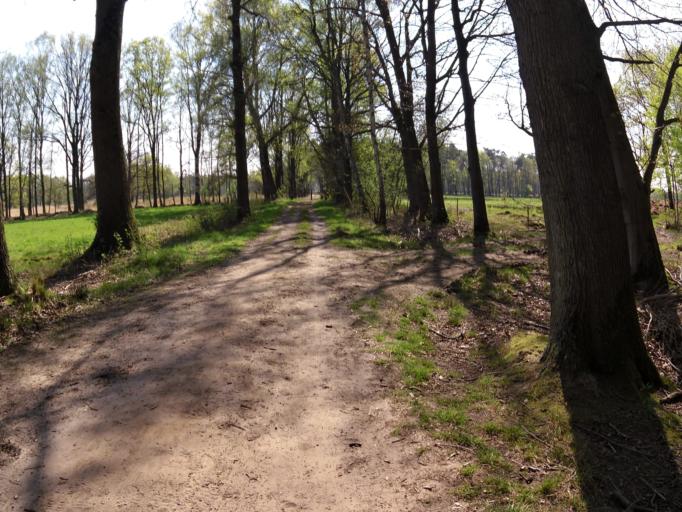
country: NL
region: North Brabant
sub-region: Gemeente Boxtel
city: Boxtel
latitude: 51.5756
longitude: 5.2832
